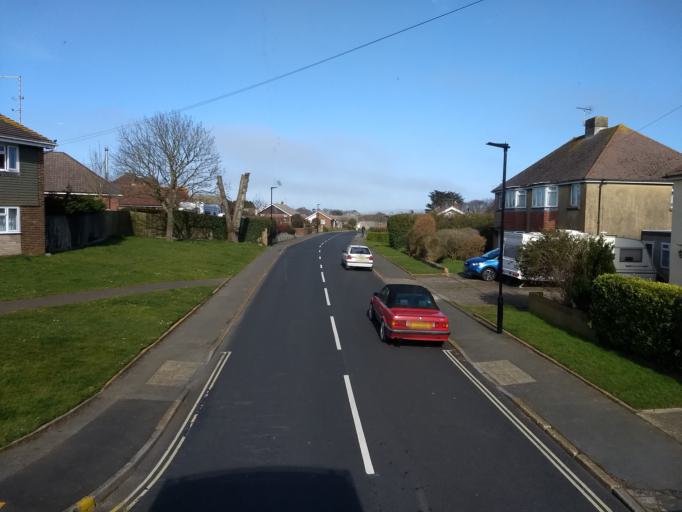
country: GB
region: England
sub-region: Isle of Wight
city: Shanklin
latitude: 50.6403
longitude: -1.1752
